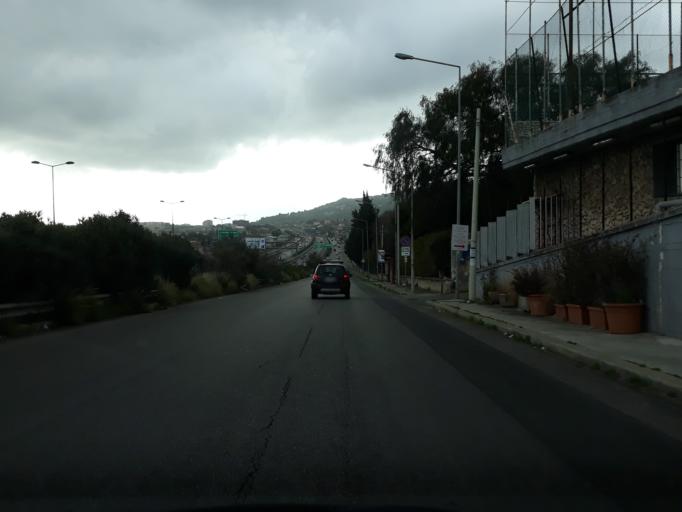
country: IT
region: Sicily
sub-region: Palermo
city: Isola delle Femmine
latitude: 38.1833
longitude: 13.2903
